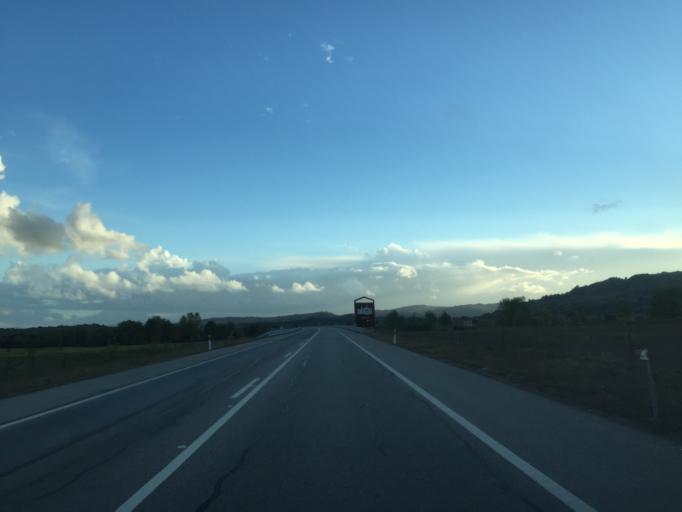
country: PT
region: Guarda
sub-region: Meda
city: Meda
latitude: 40.9220
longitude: -7.2062
